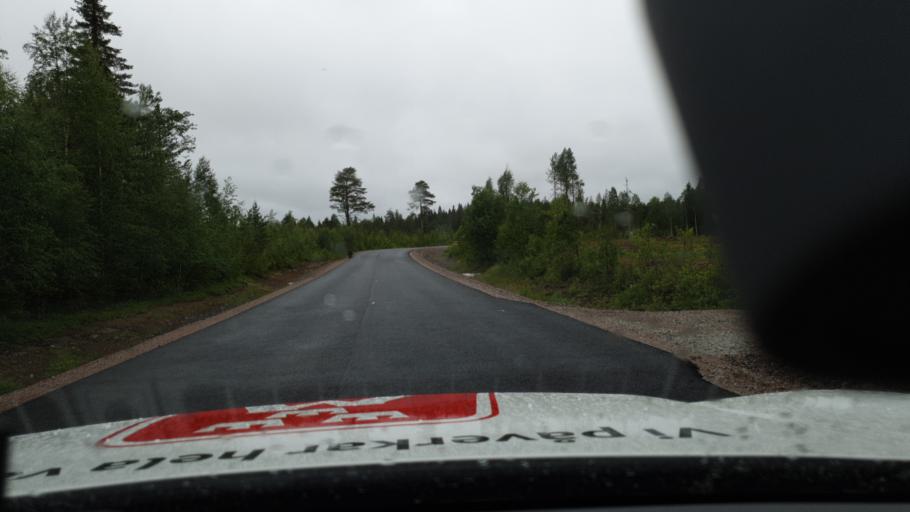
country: SE
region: Norrbotten
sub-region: Overtornea Kommun
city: OEvertornea
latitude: 66.5464
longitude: 23.3485
